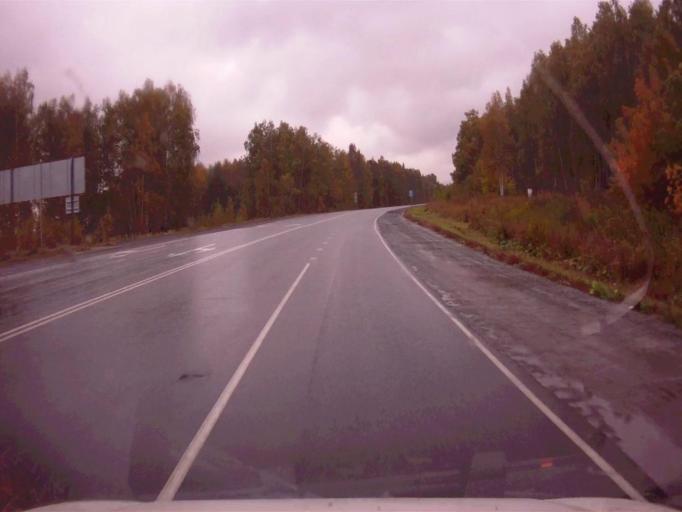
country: RU
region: Chelyabinsk
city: Roshchino
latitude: 55.3715
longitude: 61.1589
